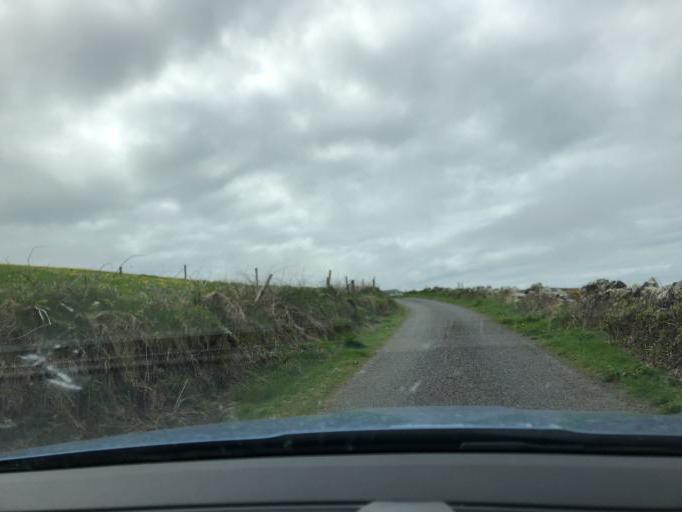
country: IE
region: Connaught
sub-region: County Galway
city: Bearna
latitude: 52.9940
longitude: -9.4042
